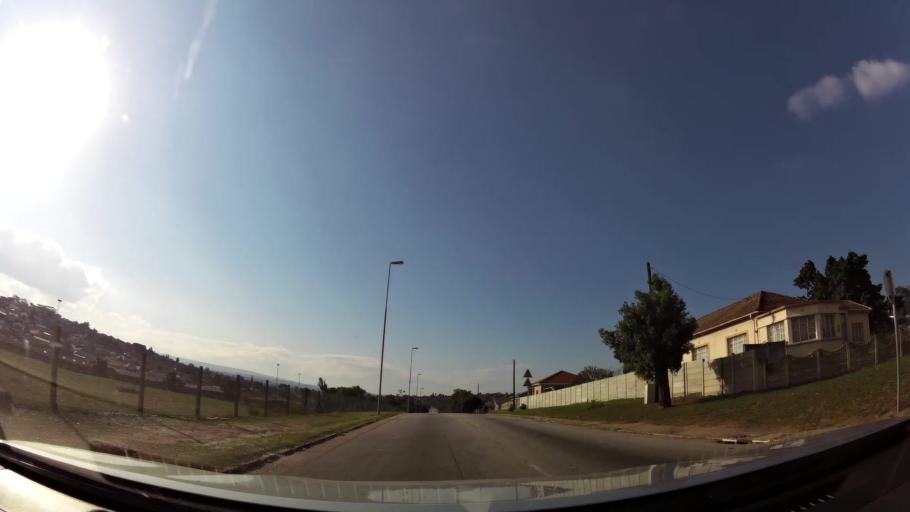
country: ZA
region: Eastern Cape
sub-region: Nelson Mandela Bay Metropolitan Municipality
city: Uitenhage
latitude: -33.7730
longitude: 25.4108
